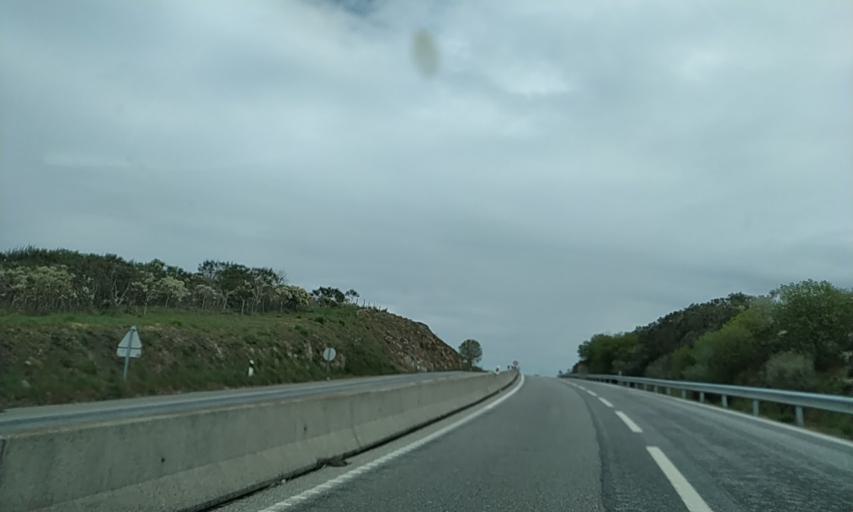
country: PT
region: Guarda
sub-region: Guarda
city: Guarda
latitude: 40.5870
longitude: -7.2734
